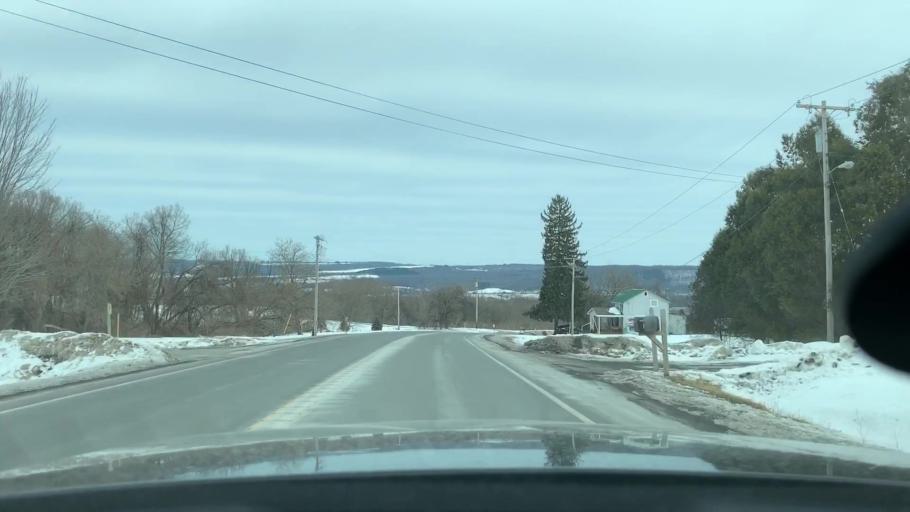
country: US
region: New York
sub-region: Herkimer County
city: Frankfort
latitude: 43.0388
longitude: -75.0956
